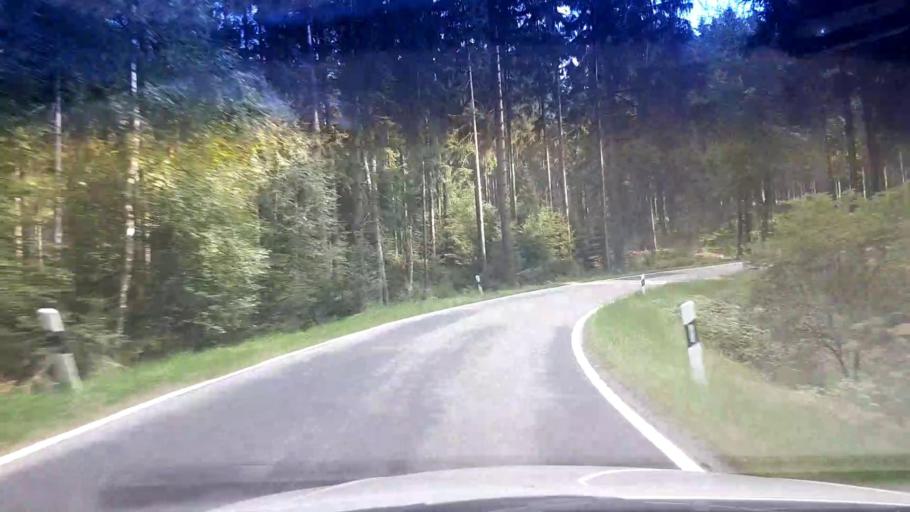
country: DE
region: Bavaria
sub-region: Upper Palatinate
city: Neualbenreuth
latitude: 49.9449
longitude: 12.4191
